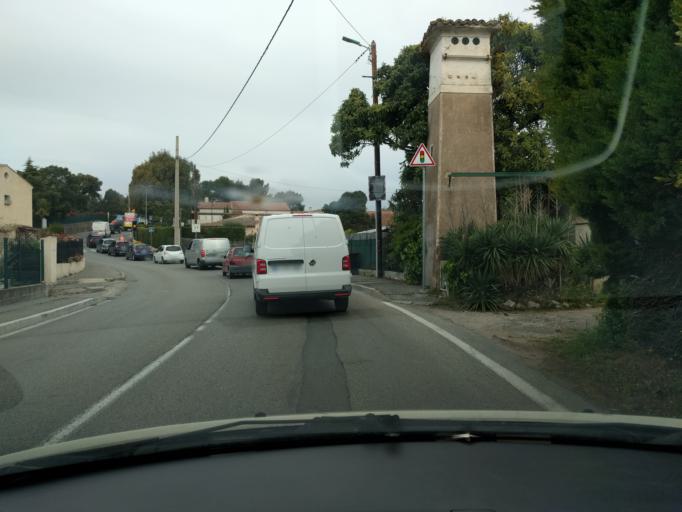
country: FR
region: Provence-Alpes-Cote d'Azur
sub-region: Departement des Alpes-Maritimes
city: La Roquette-sur-Siagne
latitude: 43.5961
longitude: 6.9560
